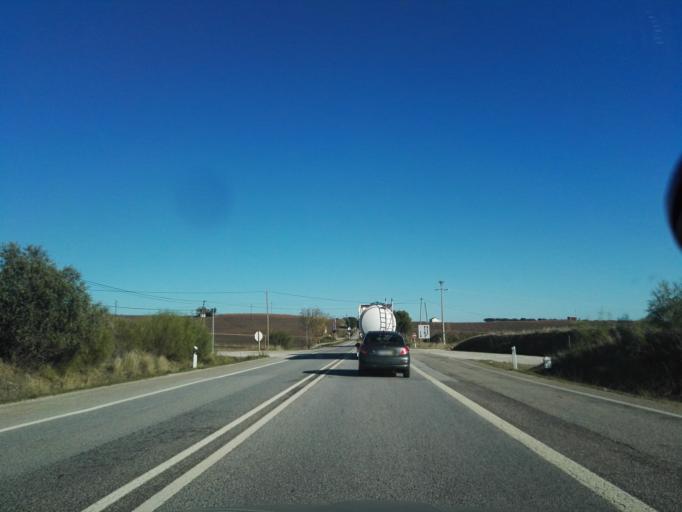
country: PT
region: Evora
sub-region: Borba
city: Borba
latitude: 38.8207
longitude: -7.4328
